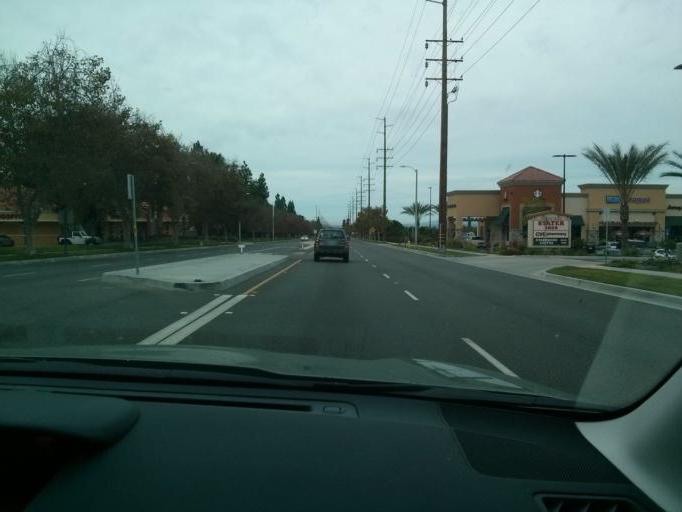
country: US
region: California
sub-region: San Bernardino County
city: Mentone
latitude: 34.0702
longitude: -117.1398
